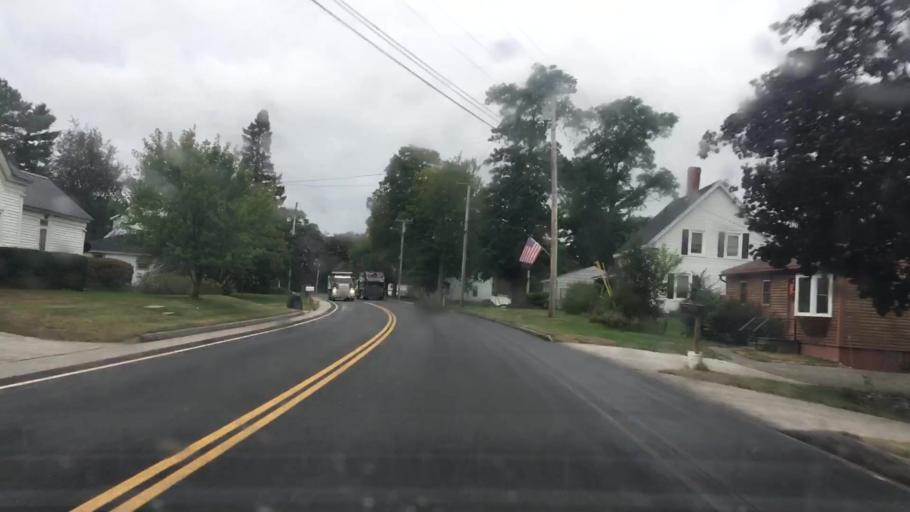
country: US
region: Maine
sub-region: Penobscot County
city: Orrington
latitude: 44.7495
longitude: -68.8062
